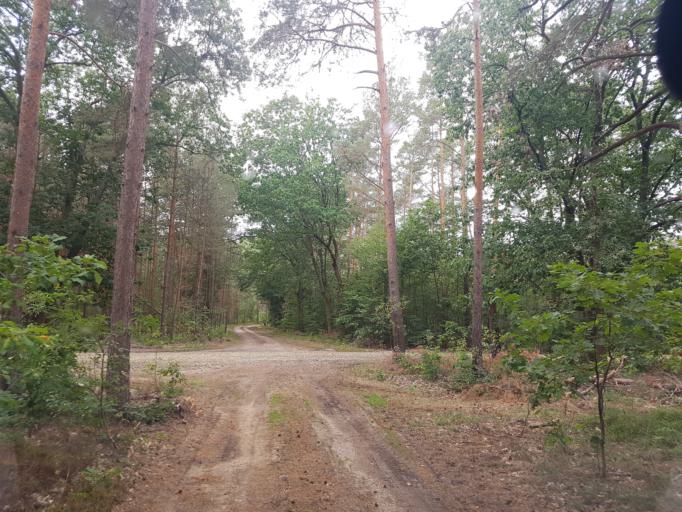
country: DE
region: Brandenburg
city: Schonborn
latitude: 51.5693
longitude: 13.4802
